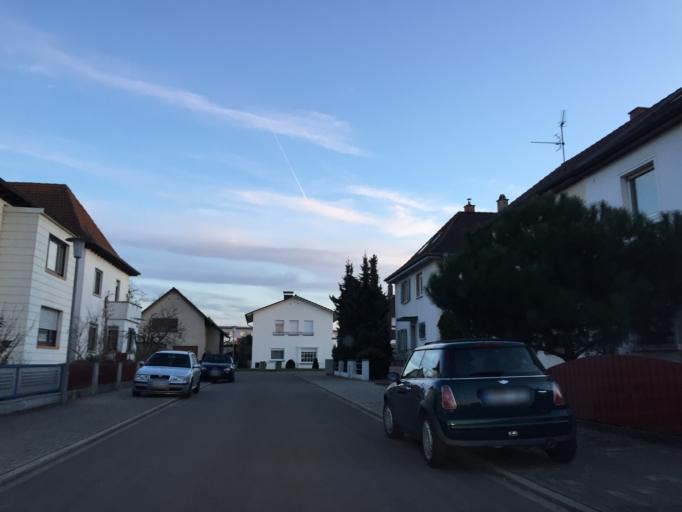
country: DE
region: Baden-Wuerttemberg
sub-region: Karlsruhe Region
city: Schwetzingen
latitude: 49.3745
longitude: 8.5763
